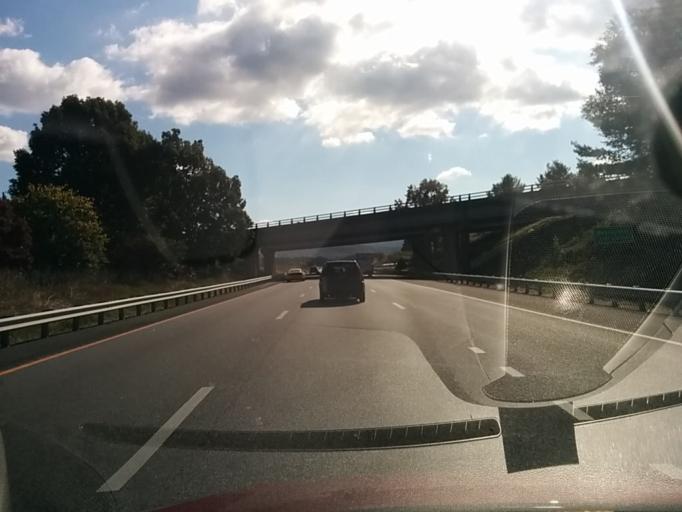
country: US
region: Virginia
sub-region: Augusta County
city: Lyndhurst
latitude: 38.0613
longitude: -78.9427
